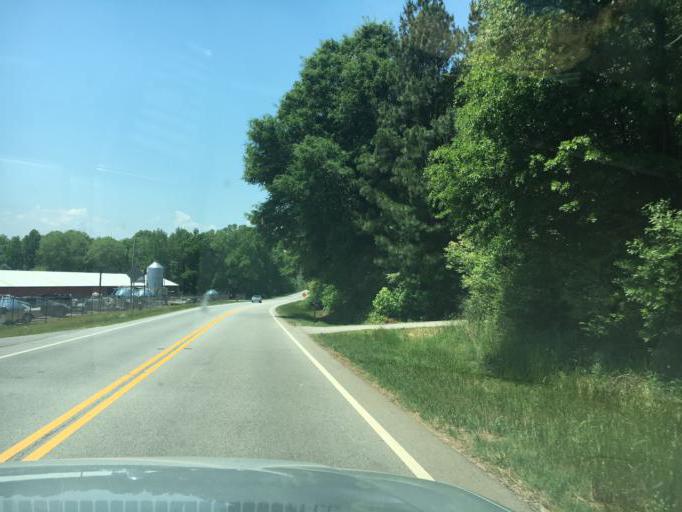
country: US
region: Georgia
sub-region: Hart County
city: Royston
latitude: 34.2901
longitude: -83.0753
